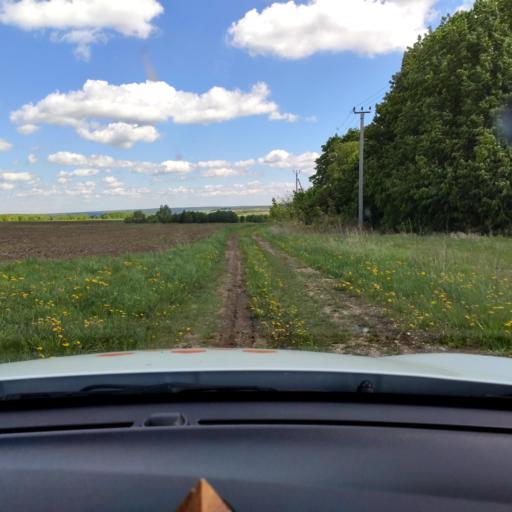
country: RU
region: Tatarstan
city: Kuybyshevskiy Zaton
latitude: 55.2648
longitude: 49.1481
